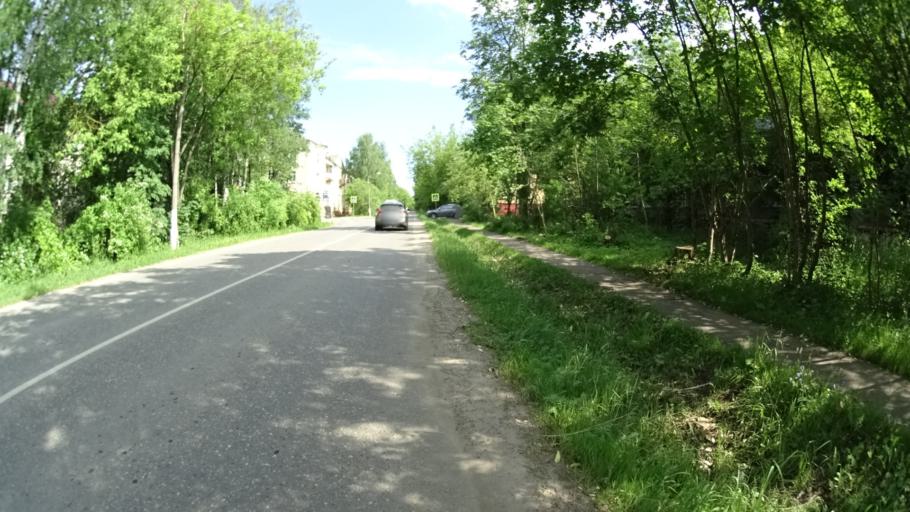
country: RU
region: Moskovskaya
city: Lesnoy
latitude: 56.0780
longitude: 37.9275
